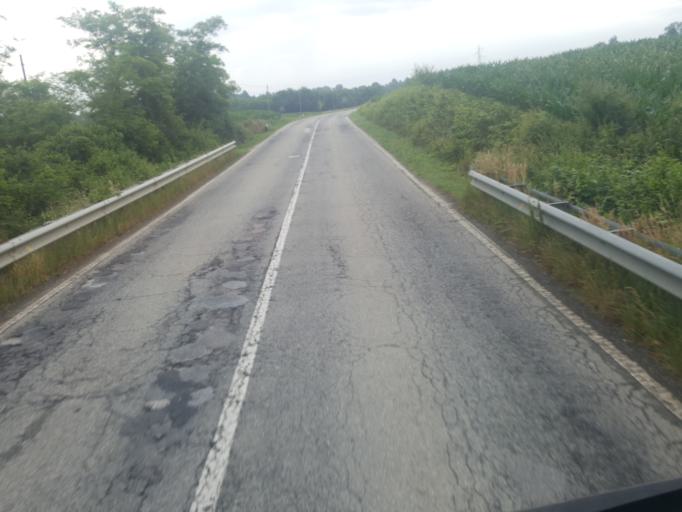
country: IT
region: Piedmont
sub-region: Provincia di Torino
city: Favari-Avatanei
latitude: 44.8552
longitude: 7.8020
